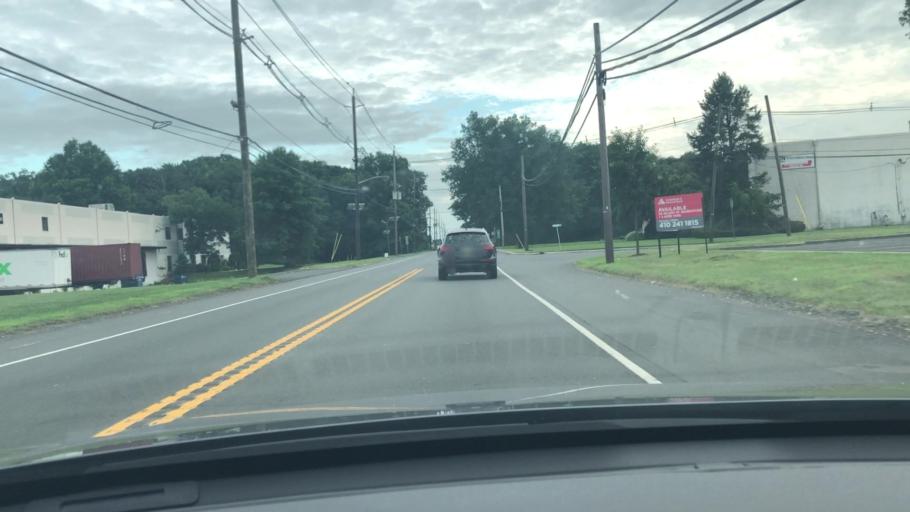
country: US
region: New Jersey
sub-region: Somerset County
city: Somerset
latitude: 40.4660
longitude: -74.4806
